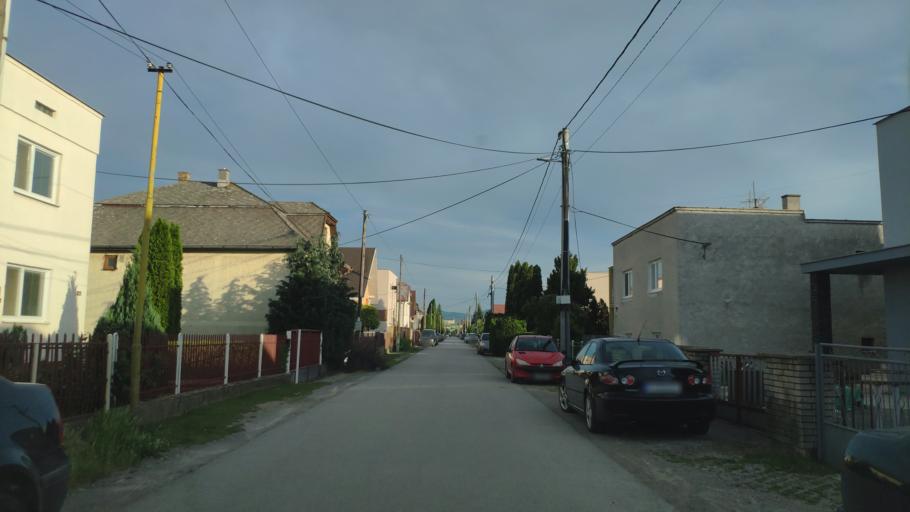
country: SK
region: Kosicky
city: Kosice
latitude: 48.6185
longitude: 21.3227
